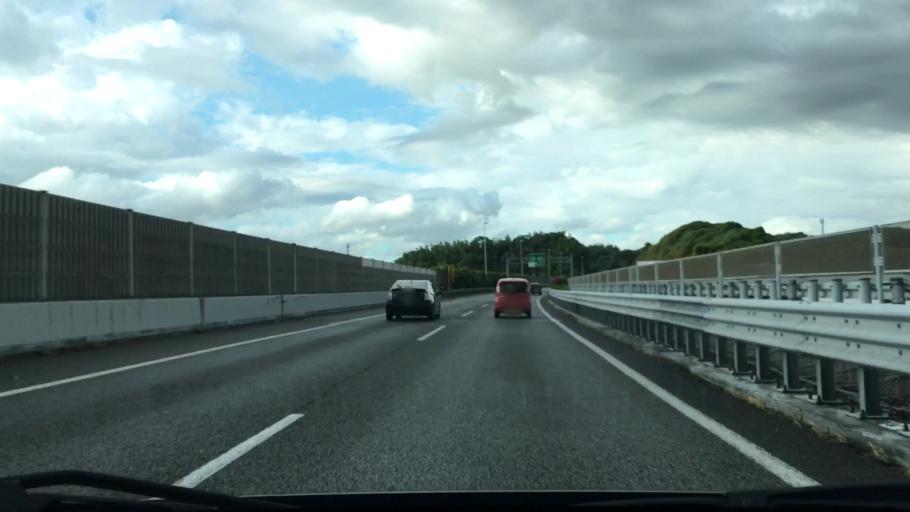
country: JP
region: Fukuoka
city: Koga
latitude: 33.7142
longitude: 130.4903
